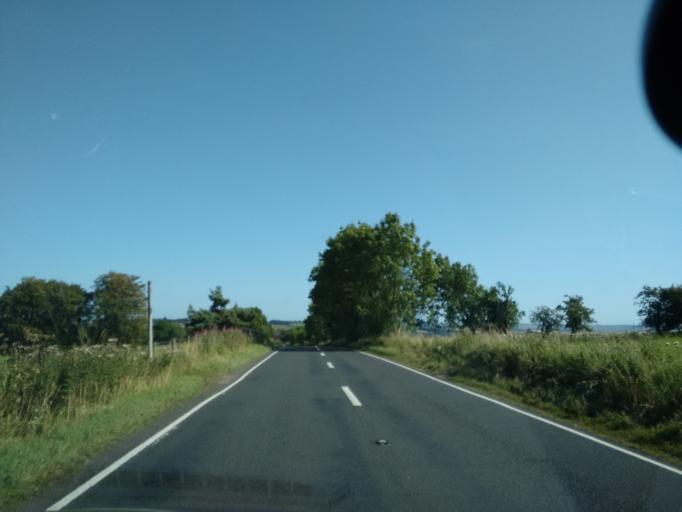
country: GB
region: England
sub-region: Northumberland
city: Corbridge
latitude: 55.0136
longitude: -2.0280
